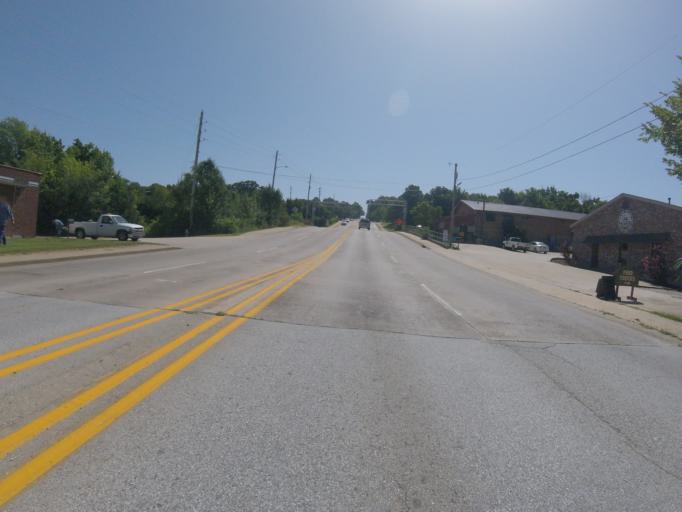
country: US
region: Arkansas
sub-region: Washington County
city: Fayetteville
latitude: 36.0774
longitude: -94.1691
